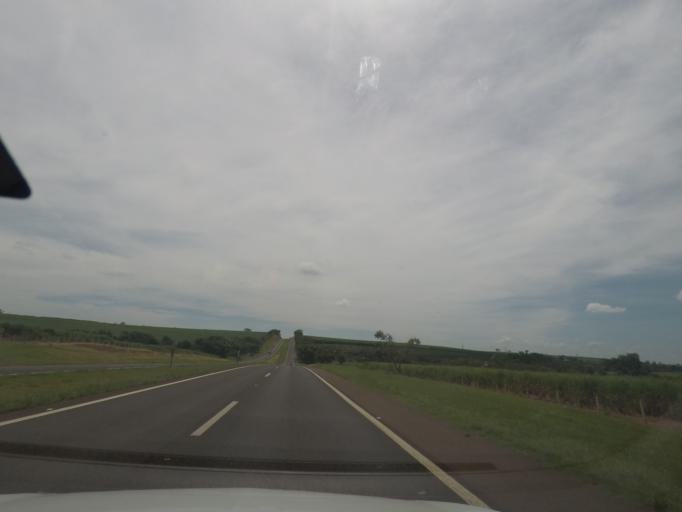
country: BR
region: Sao Paulo
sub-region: Bebedouro
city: Bebedouro
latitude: -21.0316
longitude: -48.4204
